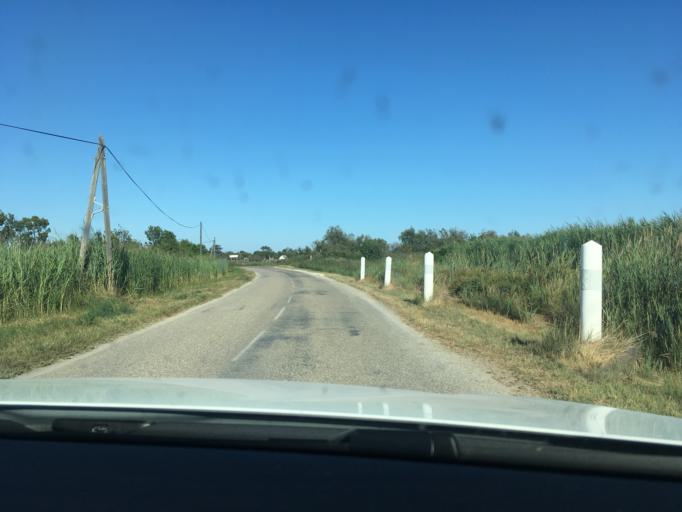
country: FR
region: Provence-Alpes-Cote d'Azur
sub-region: Departement des Bouches-du-Rhone
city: Saintes-Maries-de-la-Mer
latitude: 43.4868
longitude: 4.3784
